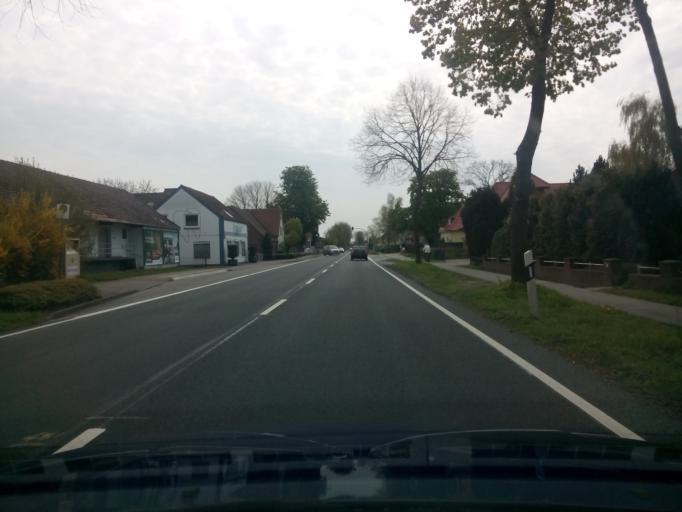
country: DE
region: Lower Saxony
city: Stuhr
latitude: 52.9927
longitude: 8.7870
